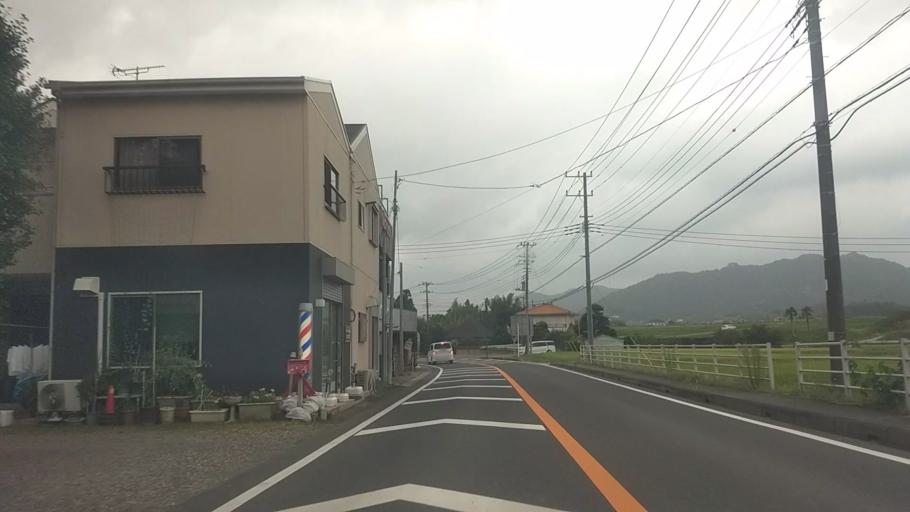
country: JP
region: Chiba
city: Kawaguchi
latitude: 35.1131
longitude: 140.0814
